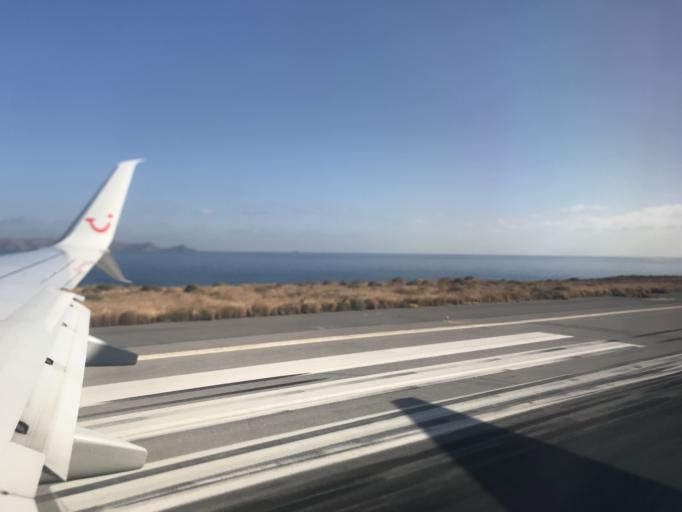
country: GR
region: Crete
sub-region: Nomos Irakleiou
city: Nea Alikarnassos
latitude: 35.3391
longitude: 25.1876
